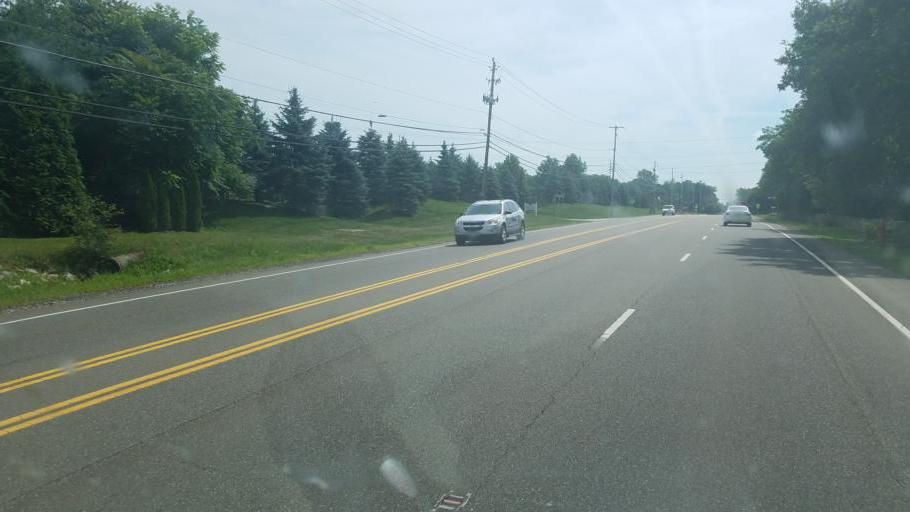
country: US
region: Ohio
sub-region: Summit County
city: Northfield
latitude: 41.3144
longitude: -81.5673
